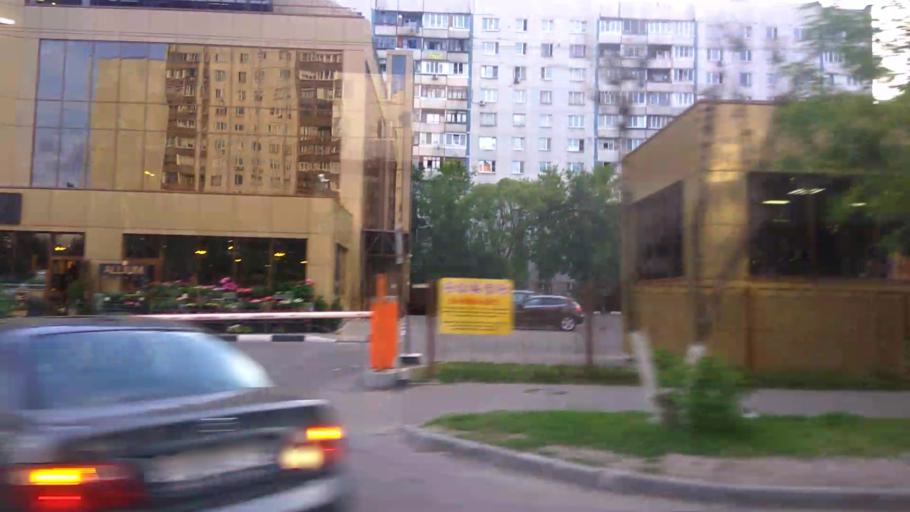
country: RU
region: Moskovskaya
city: Yubileyny
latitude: 55.9208
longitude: 37.8684
